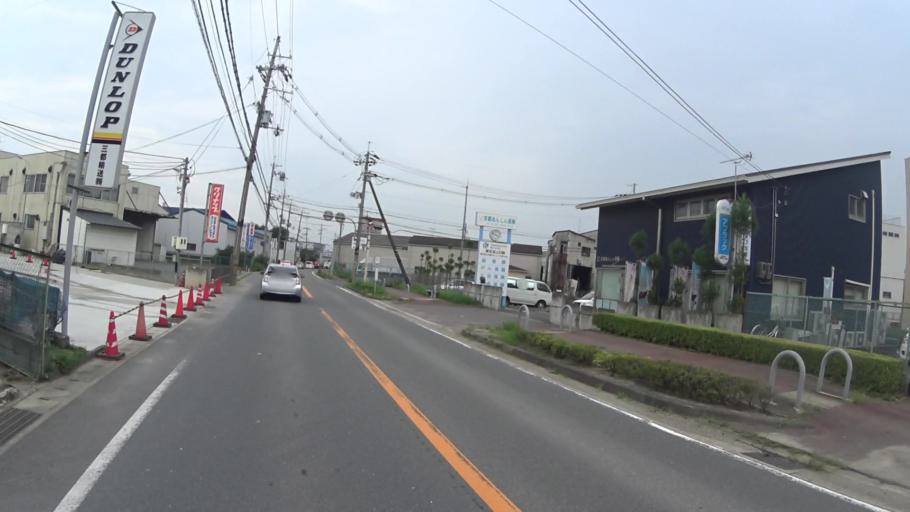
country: JP
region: Kyoto
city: Tanabe
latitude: 34.8173
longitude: 135.7679
